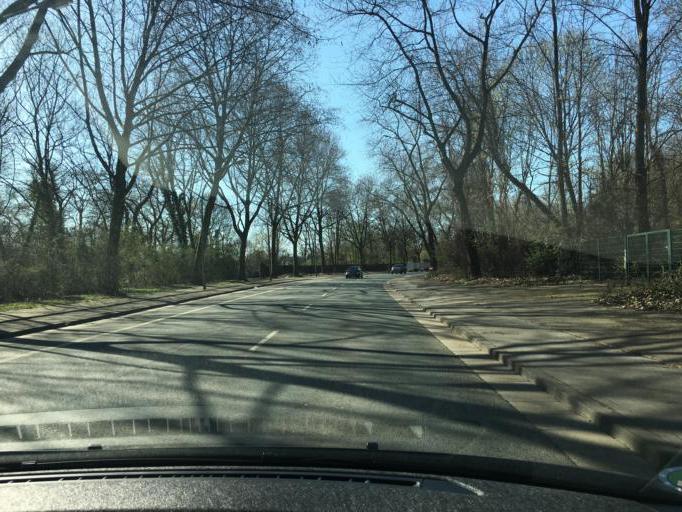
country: DE
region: North Rhine-Westphalia
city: Meiderich
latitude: 51.5055
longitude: 6.7431
